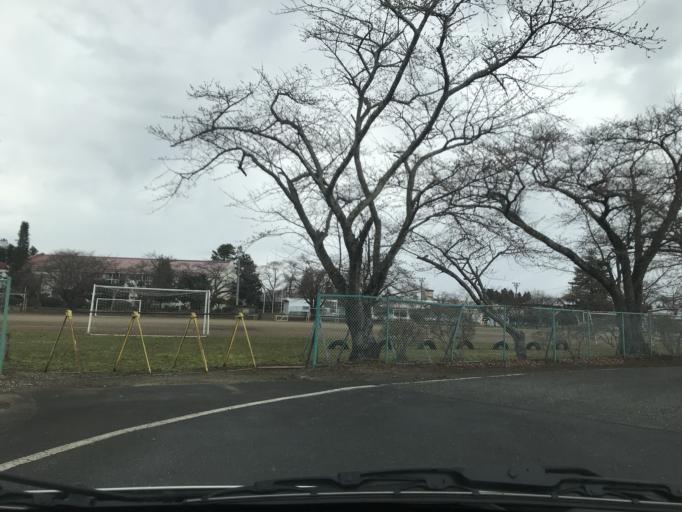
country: JP
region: Iwate
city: Mizusawa
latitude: 39.0959
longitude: 141.0803
